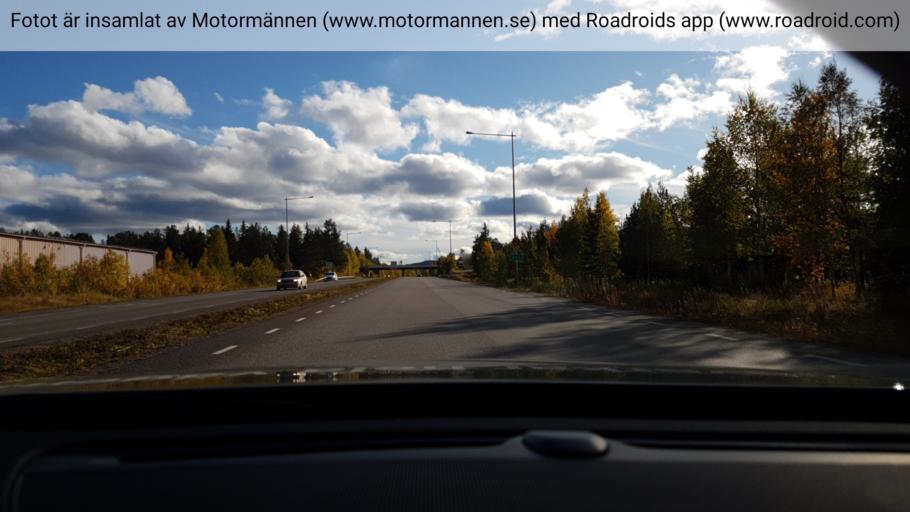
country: SE
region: Norrbotten
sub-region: Gallivare Kommun
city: Gaellivare
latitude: 67.1452
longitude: 20.6633
